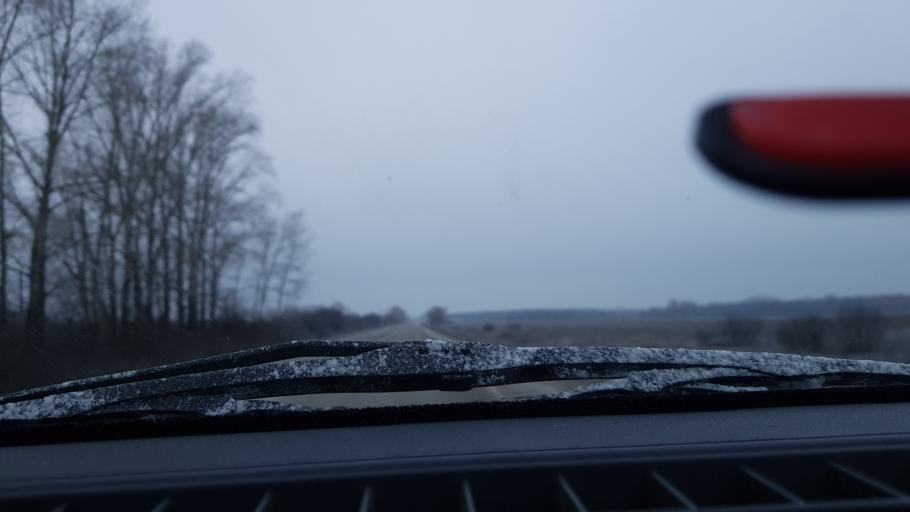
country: RU
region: Ulyanovsk
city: Novaya Mayna
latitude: 54.1706
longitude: 49.6910
